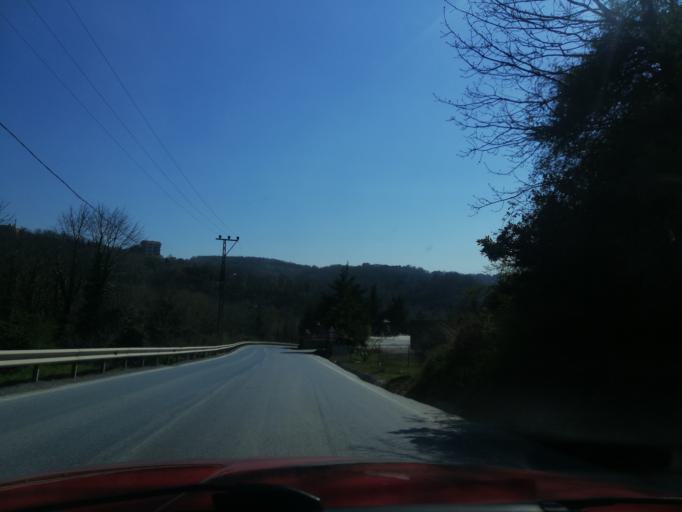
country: TR
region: Istanbul
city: Mahmut Sevket Pasa
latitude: 41.1018
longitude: 29.1588
